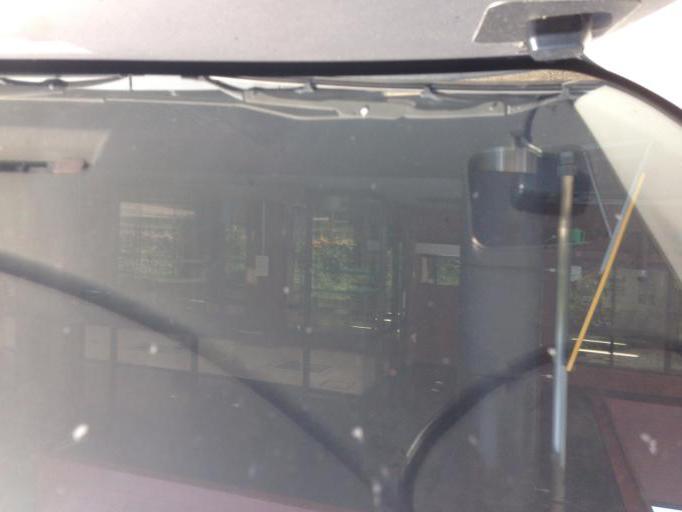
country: JP
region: Fukushima
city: Kitakata
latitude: 37.4692
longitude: 139.9384
